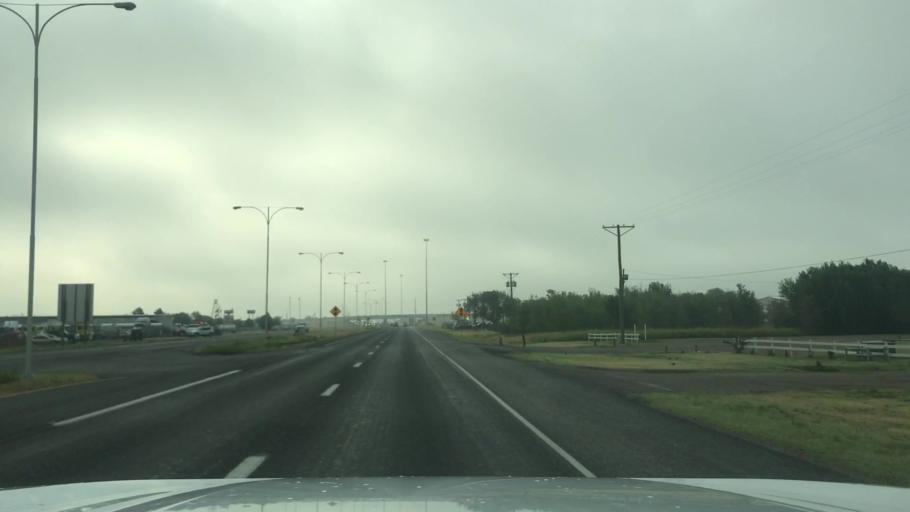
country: US
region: Texas
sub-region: Lubbock County
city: Lubbock
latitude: 33.5316
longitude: -101.8259
